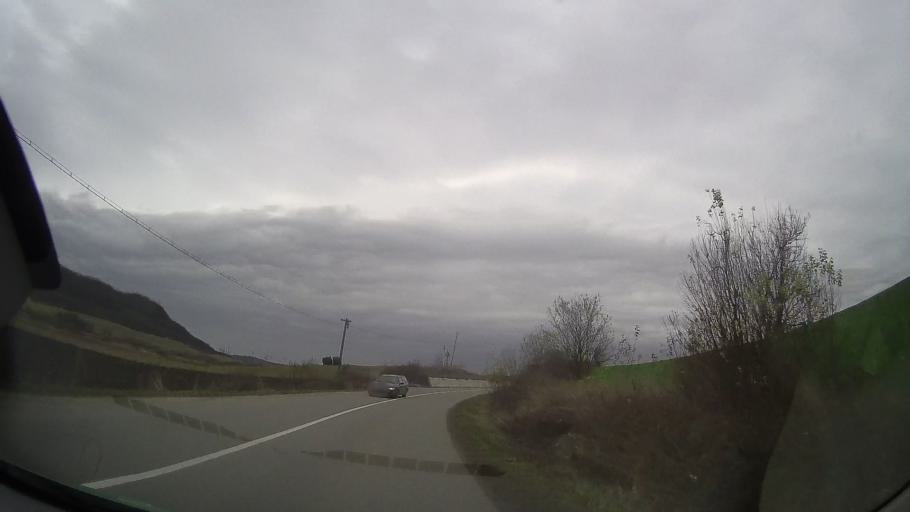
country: RO
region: Bistrita-Nasaud
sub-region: Comuna Milas
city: Milas
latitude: 46.8002
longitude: 24.4281
